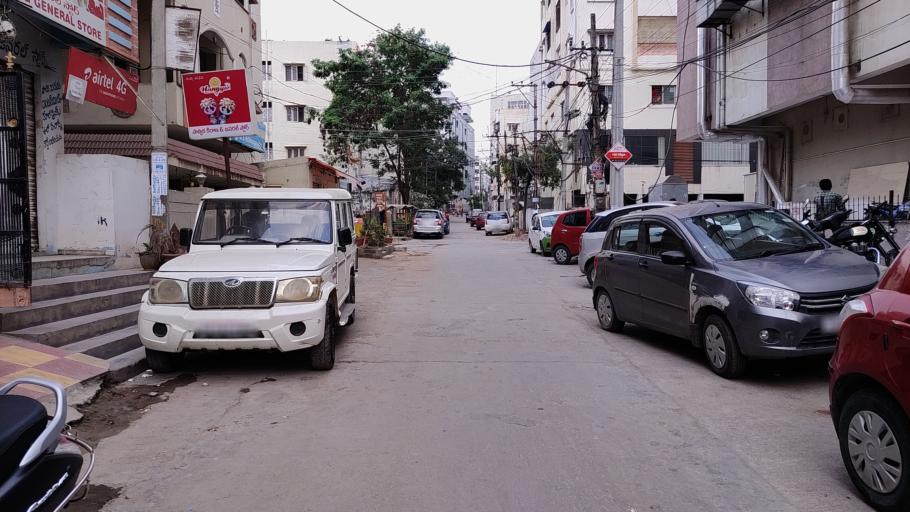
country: IN
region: Telangana
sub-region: Rangareddi
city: Gaddi Annaram
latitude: 17.3649
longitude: 78.5440
